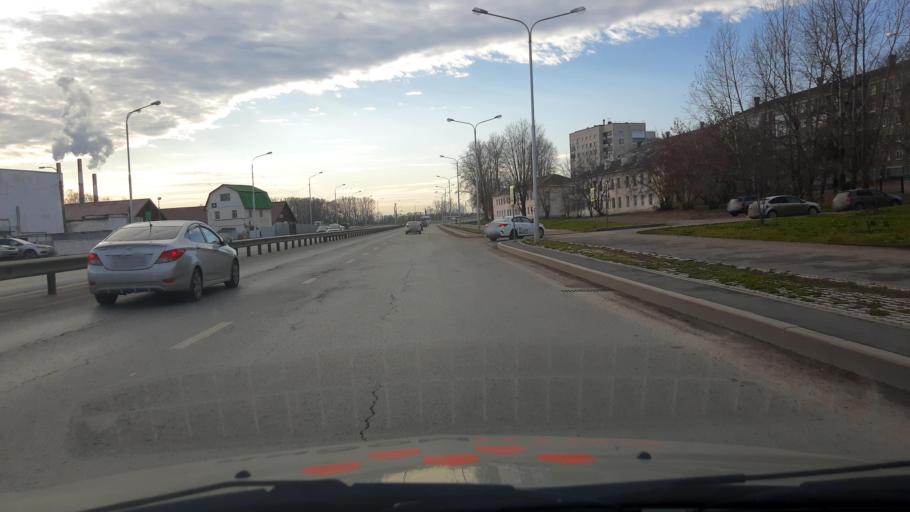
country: RU
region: Bashkortostan
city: Ufa
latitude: 54.8018
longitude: 56.1349
